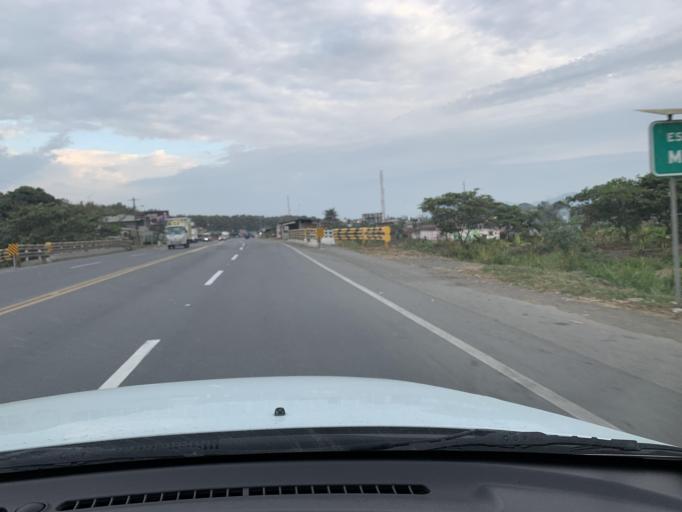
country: EC
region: Guayas
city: Yaguachi Nuevo
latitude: -2.2448
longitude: -79.6366
